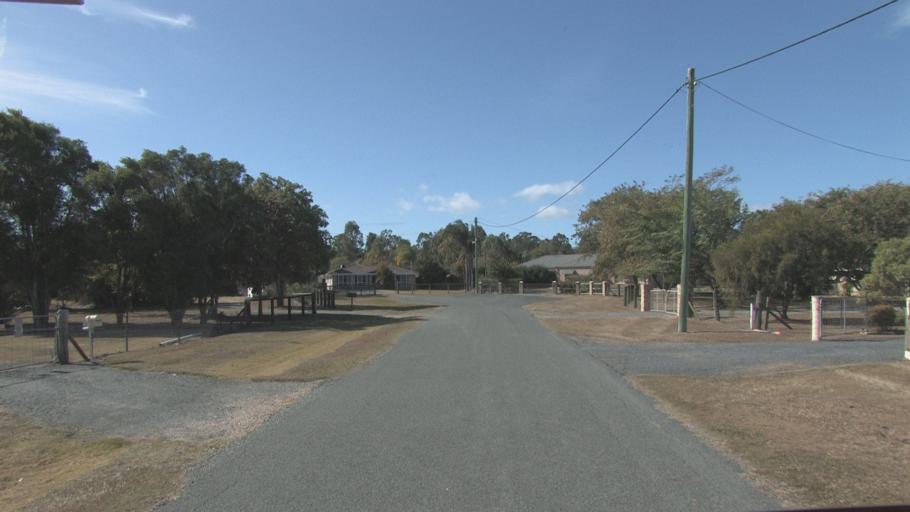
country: AU
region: Queensland
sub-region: Logan
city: Cedar Vale
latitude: -27.8641
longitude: 152.9665
